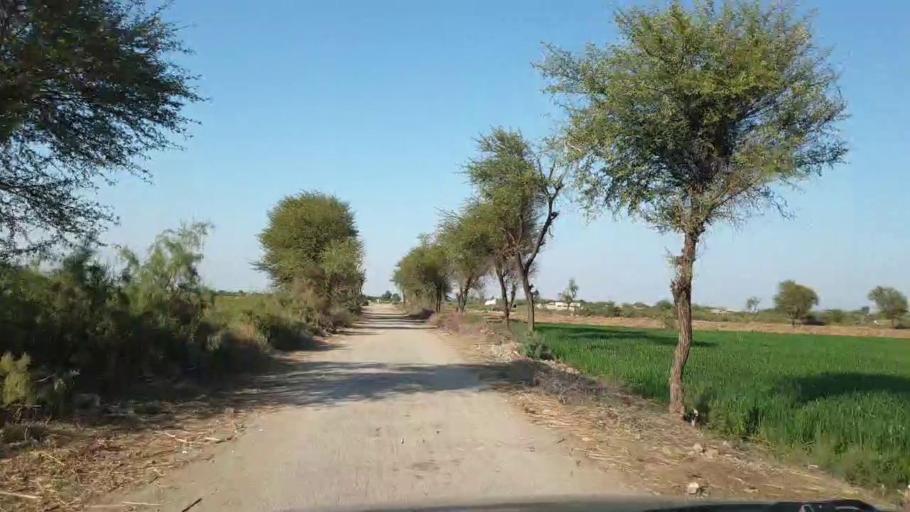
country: PK
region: Sindh
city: Khadro
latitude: 26.2044
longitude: 68.7543
